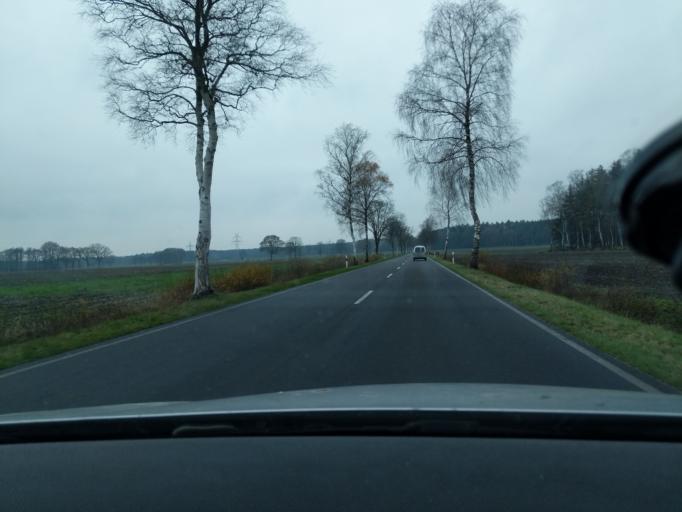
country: DE
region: Lower Saxony
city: Harsefeld
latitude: 53.4107
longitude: 9.5334
